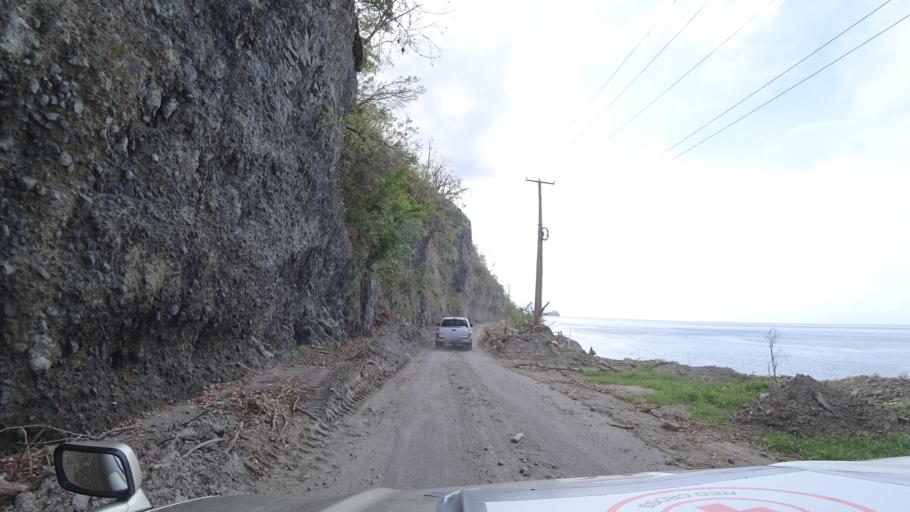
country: DM
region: Saint Luke
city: Pointe Michel
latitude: 15.2554
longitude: -61.3758
